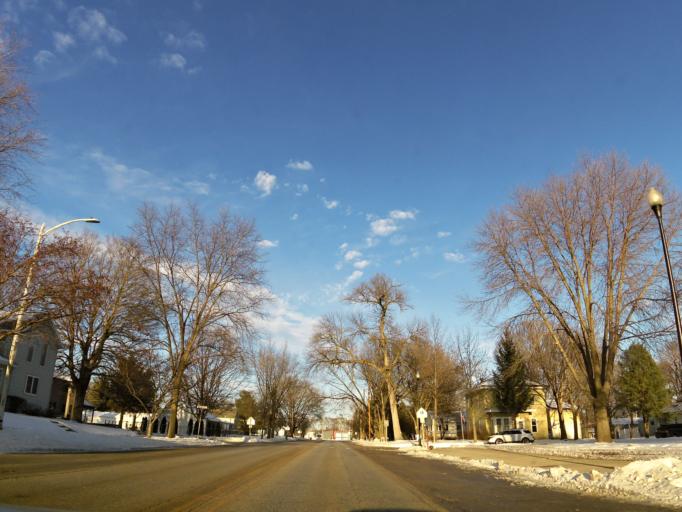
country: US
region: Iowa
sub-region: Butler County
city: Shell Rock
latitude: 42.7126
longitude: -92.5803
